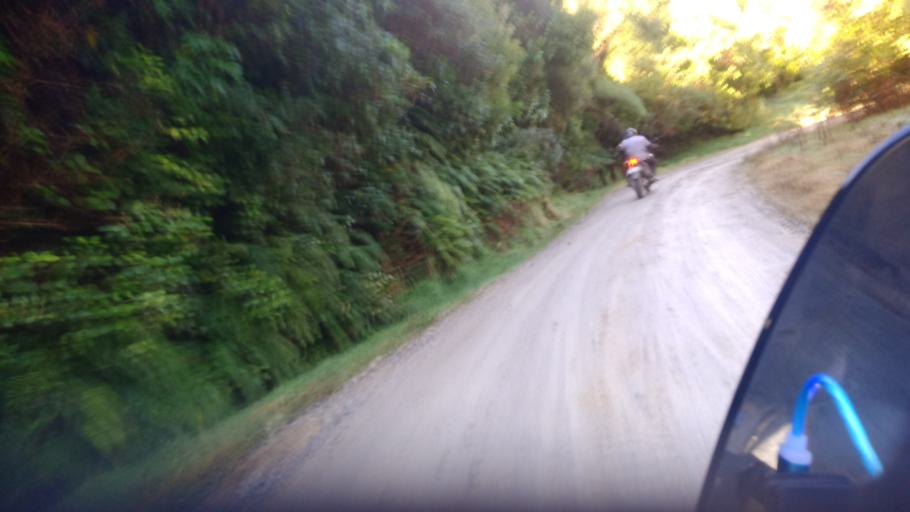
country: NZ
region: Hawke's Bay
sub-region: Wairoa District
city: Wairoa
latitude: -38.6661
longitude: 177.5300
